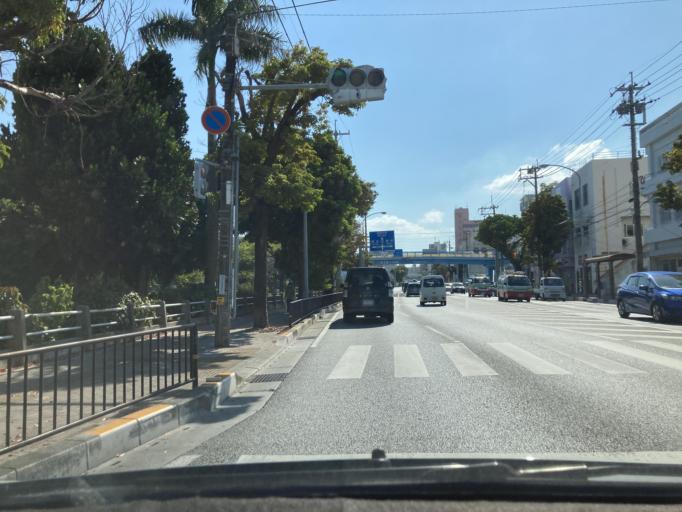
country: JP
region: Okinawa
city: Naha-shi
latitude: 26.2089
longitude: 127.6919
